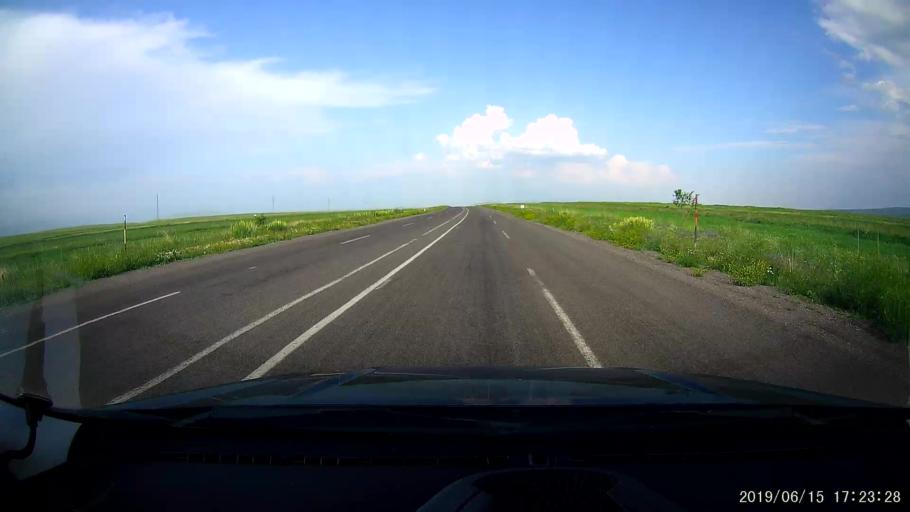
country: TR
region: Kars
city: Basgedikler
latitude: 40.6167
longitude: 43.3634
